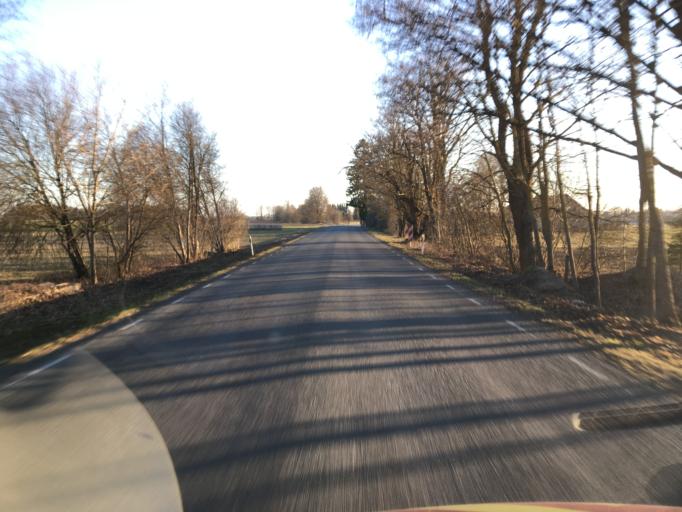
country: EE
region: Raplamaa
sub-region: Kehtna vald
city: Kehtna
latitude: 59.0428
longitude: 24.9424
